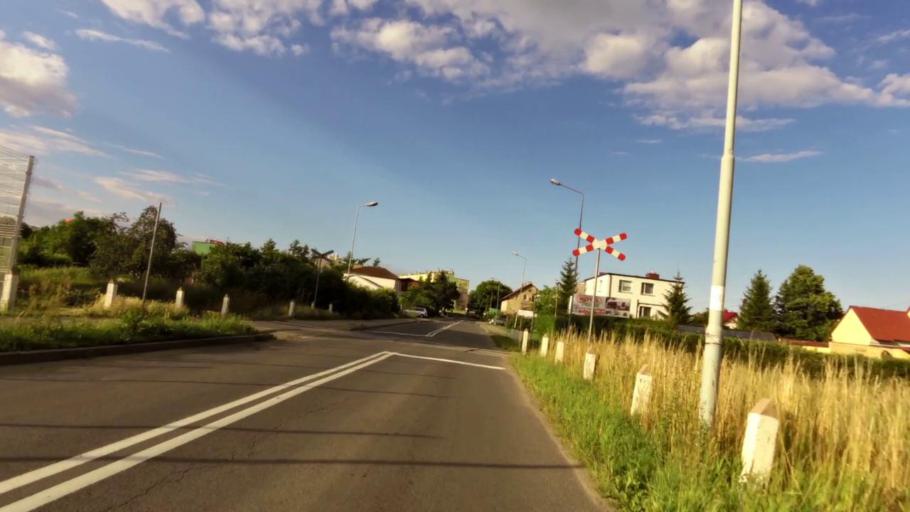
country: PL
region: West Pomeranian Voivodeship
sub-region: Powiat slawienski
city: Darlowo
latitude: 54.4144
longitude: 16.4072
